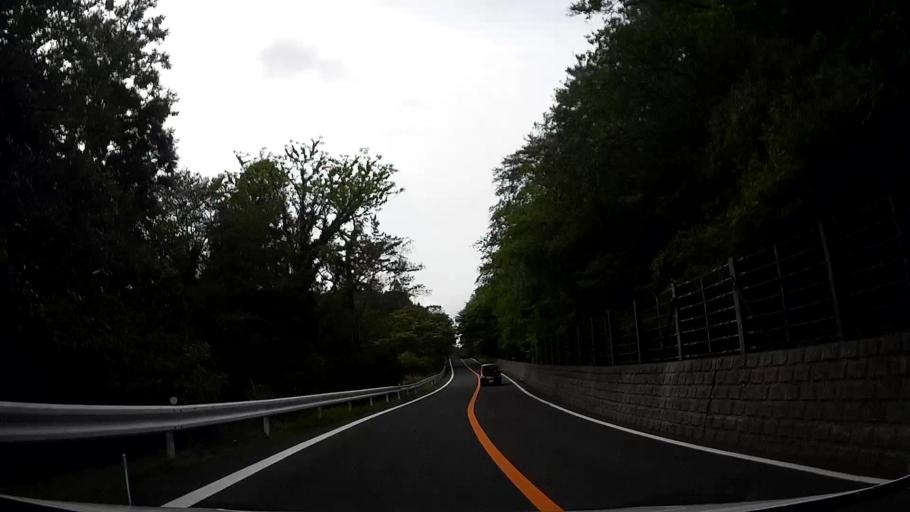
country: JP
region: Shizuoka
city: Ito
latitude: 34.9840
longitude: 139.0498
